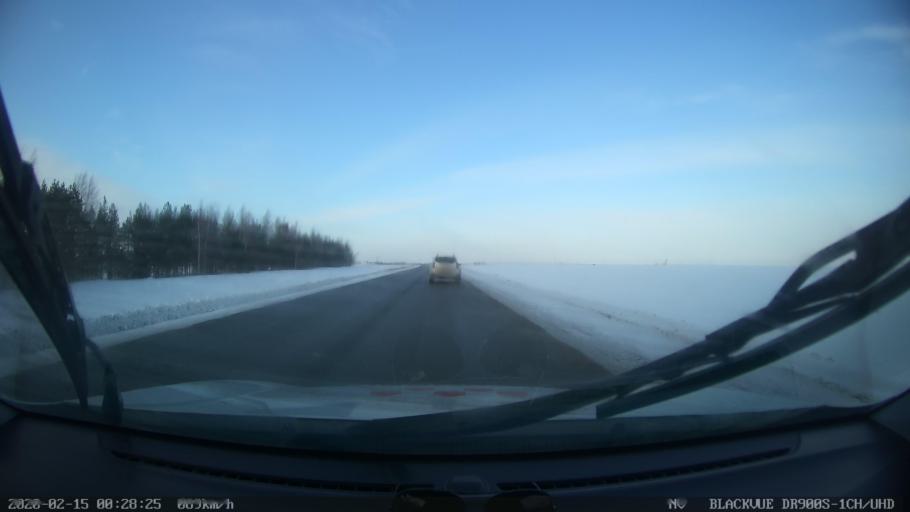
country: RU
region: Tatarstan
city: Verkhniy Uslon
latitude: 55.6422
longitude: 48.8761
